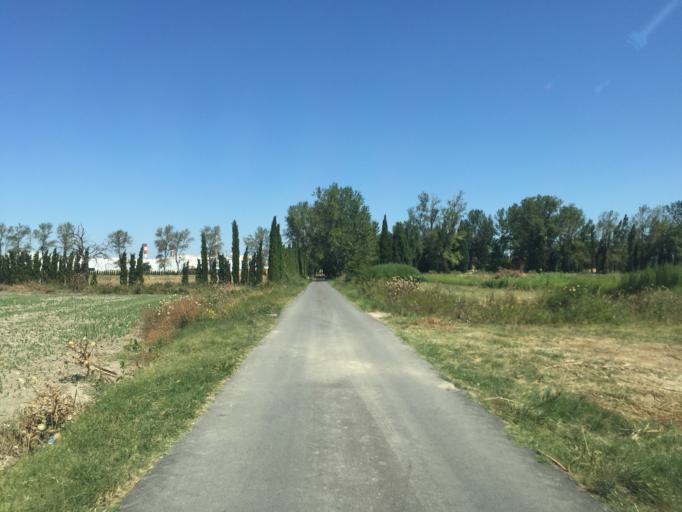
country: FR
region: Provence-Alpes-Cote d'Azur
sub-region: Departement du Vaucluse
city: Orange
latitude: 44.1238
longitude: 4.8461
